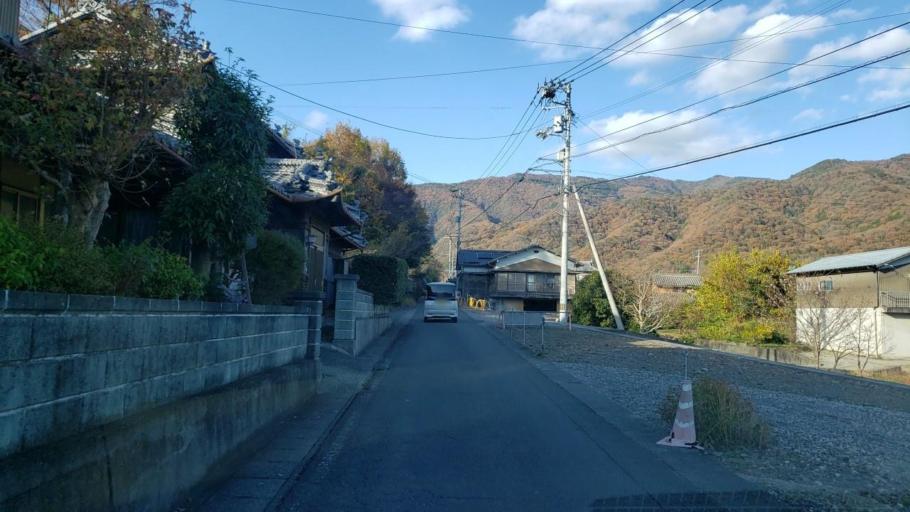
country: JP
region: Tokushima
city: Wakimachi
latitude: 34.0639
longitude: 134.0878
